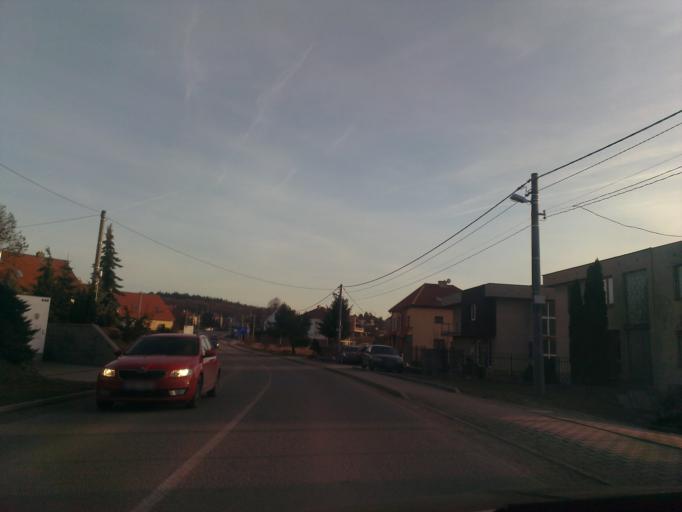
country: CZ
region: South Moravian
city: Bilovice nad Svitavou
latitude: 49.2532
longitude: 16.7320
